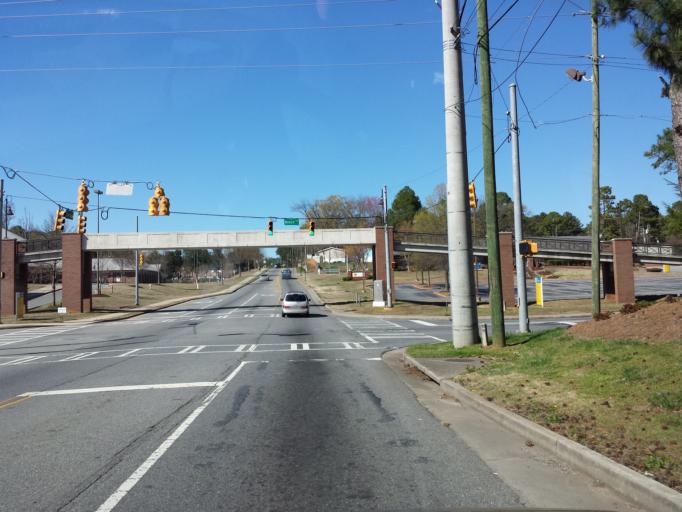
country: US
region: Georgia
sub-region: Cobb County
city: Fair Oaks
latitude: 33.9284
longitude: -84.5549
